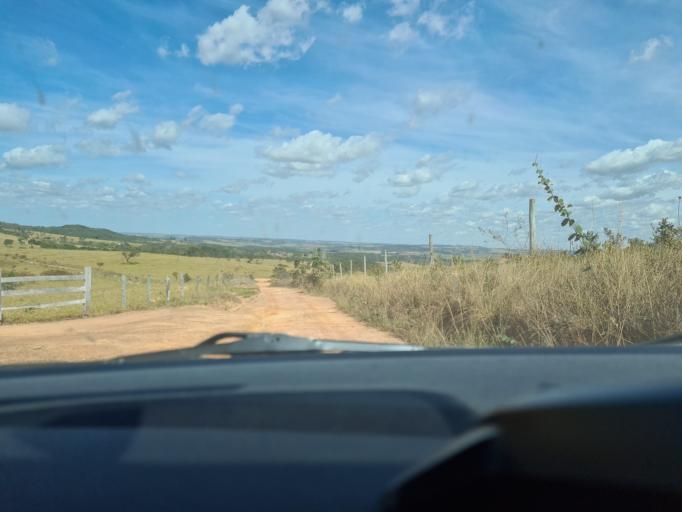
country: BR
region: Goias
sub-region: Silvania
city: Silvania
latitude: -16.5374
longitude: -48.5544
